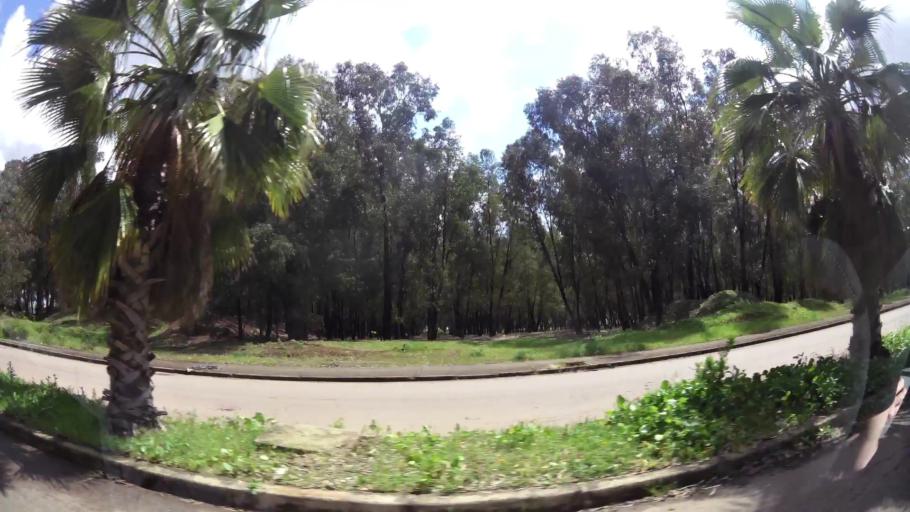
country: MA
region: Grand Casablanca
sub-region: Mediouna
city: Mediouna
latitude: 33.4002
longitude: -7.5571
